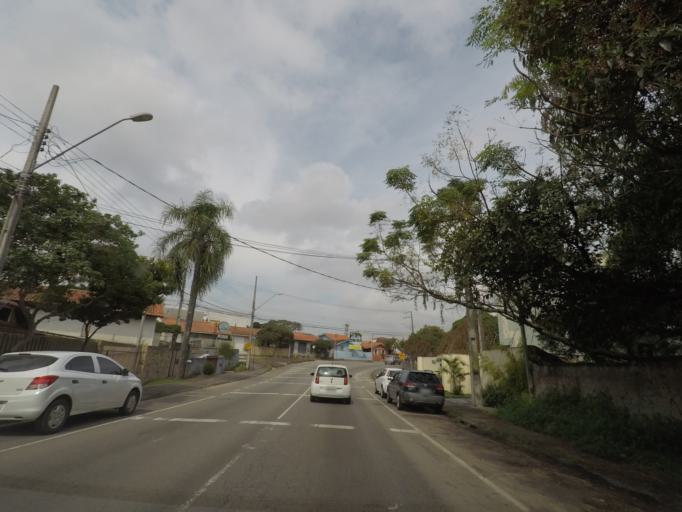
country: BR
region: Parana
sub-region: Curitiba
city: Curitiba
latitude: -25.4936
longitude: -49.2869
